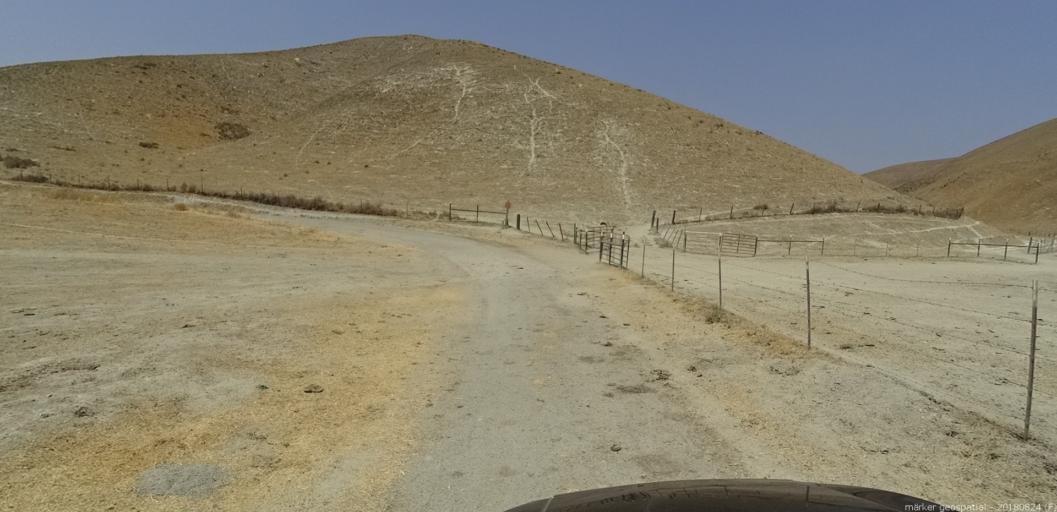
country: US
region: California
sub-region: Monterey County
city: King City
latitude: 36.2013
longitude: -120.9414
